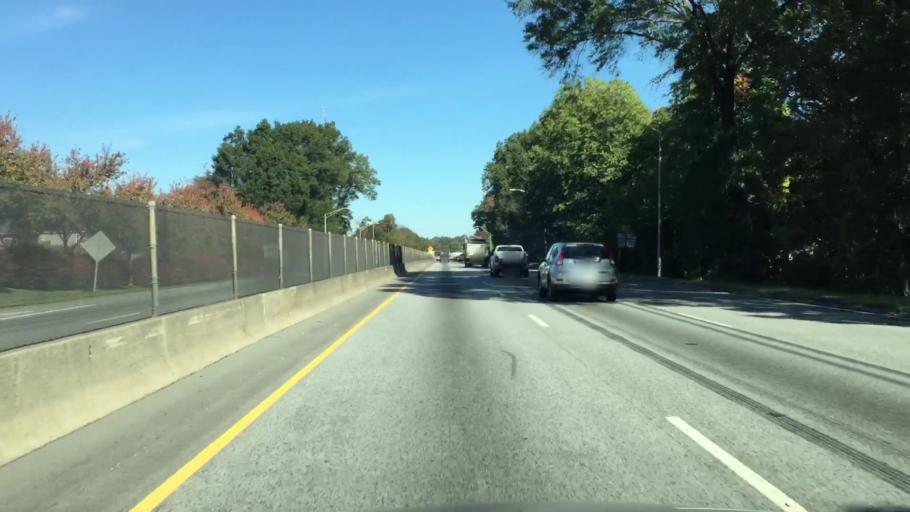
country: US
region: North Carolina
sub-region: Guilford County
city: Greensboro
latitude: 36.0757
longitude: -79.7666
